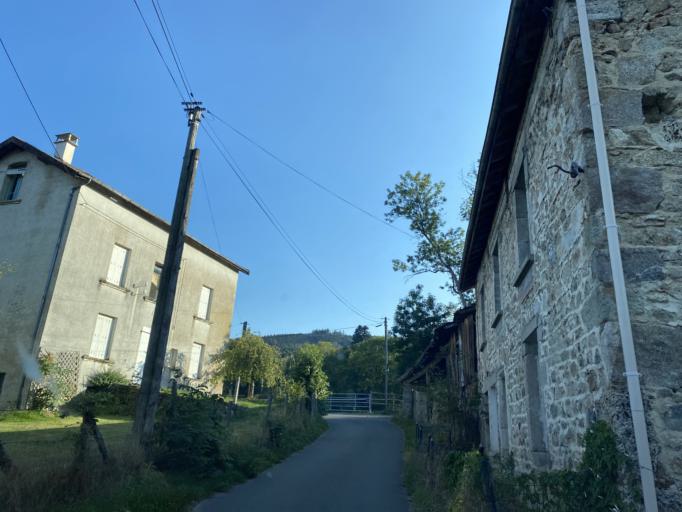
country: FR
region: Rhone-Alpes
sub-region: Departement de la Loire
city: Noiretable
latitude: 45.8010
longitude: 3.7622
